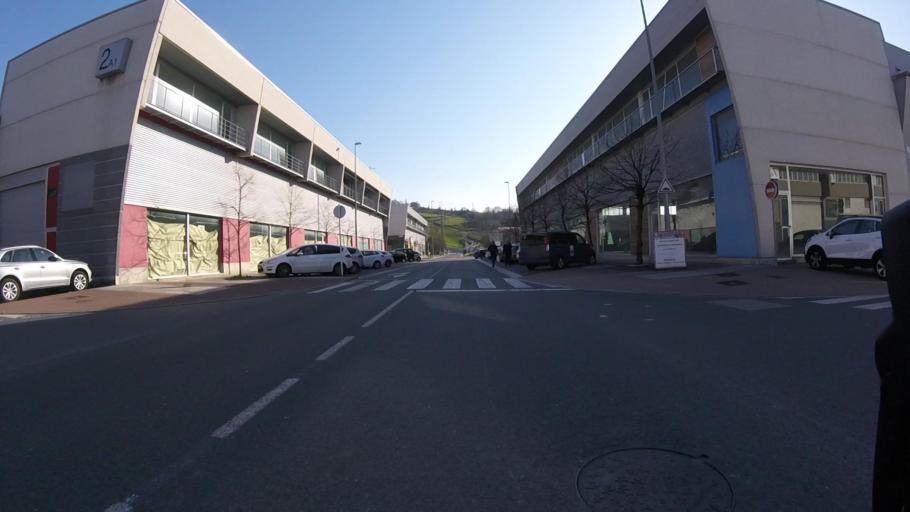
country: ES
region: Basque Country
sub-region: Provincia de Guipuzcoa
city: Astigarraga
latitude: 43.2721
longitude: -1.9549
